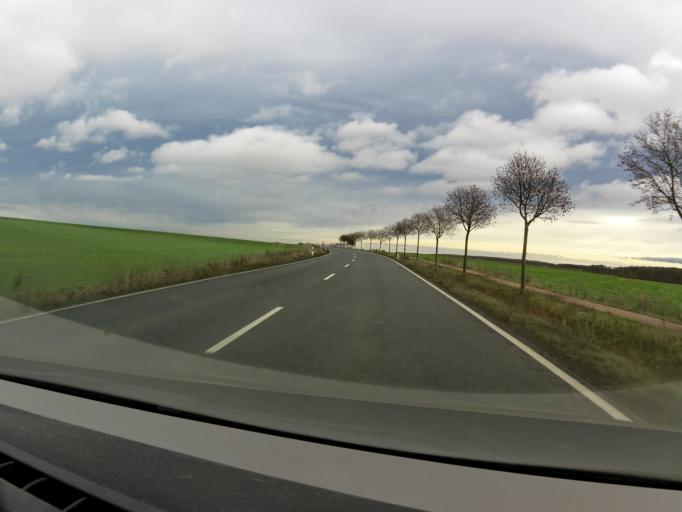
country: DE
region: Saxony-Anhalt
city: Blankenheim
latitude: 51.5407
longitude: 11.3897
